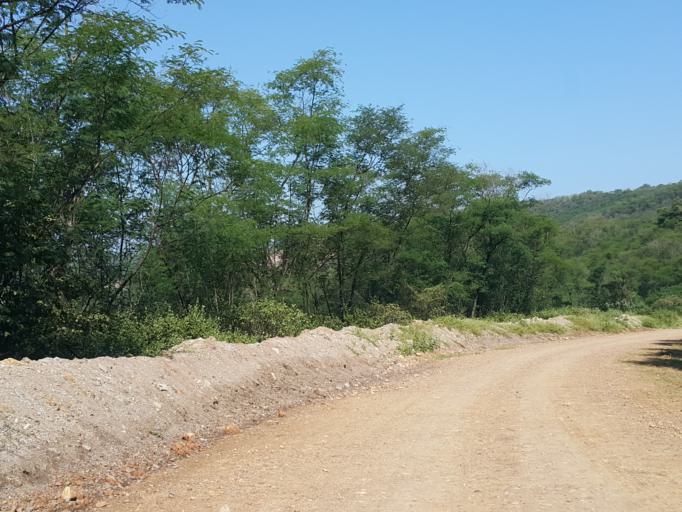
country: TH
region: Lampang
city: Mae Mo
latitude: 18.3261
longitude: 99.7394
